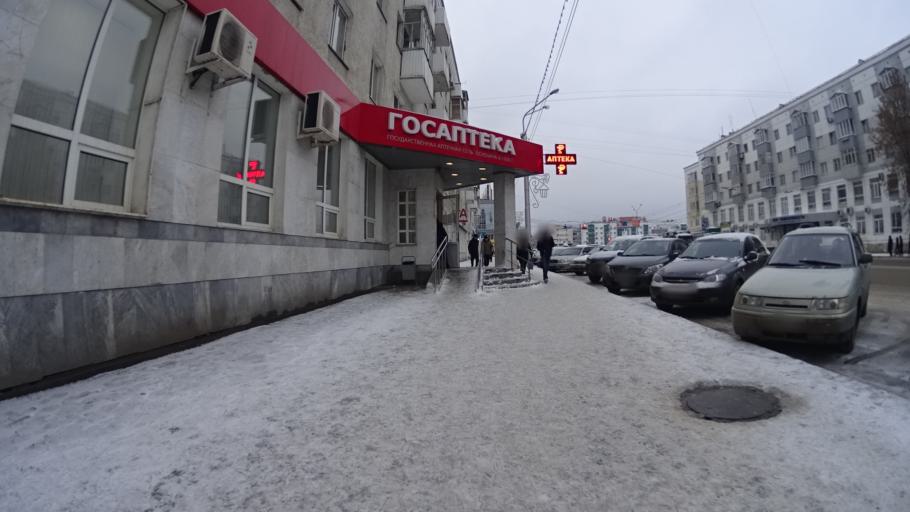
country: RU
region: Bashkortostan
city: Ufa
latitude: 54.7336
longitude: 55.9568
